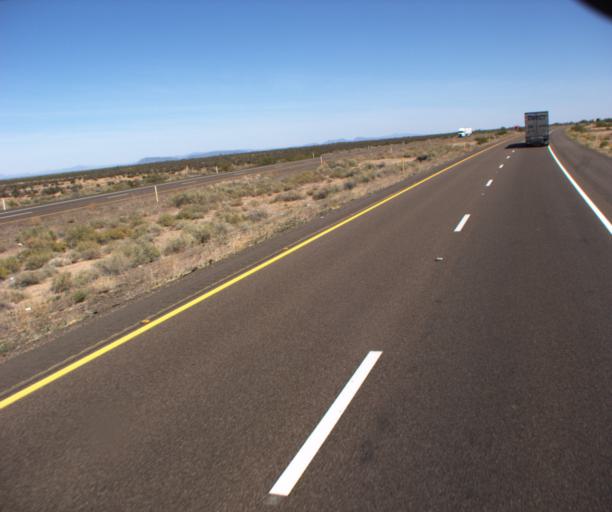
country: US
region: Arizona
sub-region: Yuma County
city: Wellton
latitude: 32.8161
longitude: -113.4996
